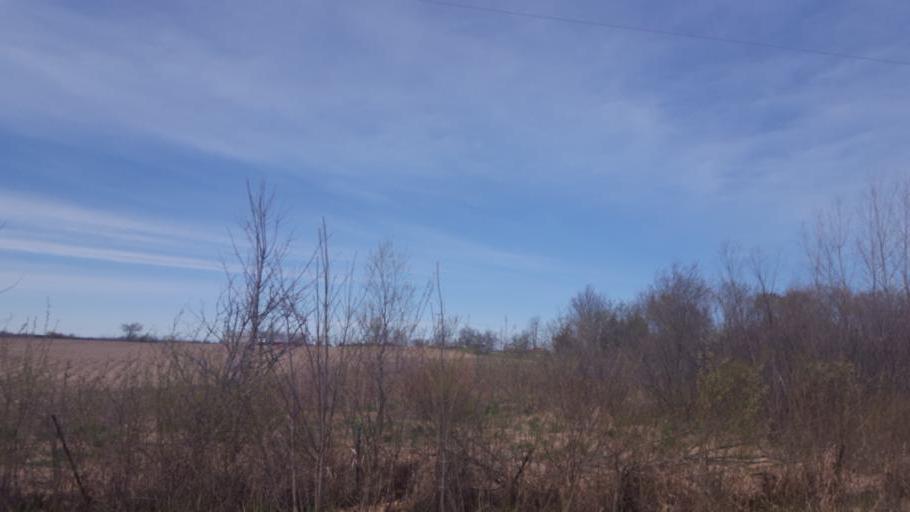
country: US
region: Michigan
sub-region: Gladwin County
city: Gladwin
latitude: 44.0598
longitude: -84.4686
